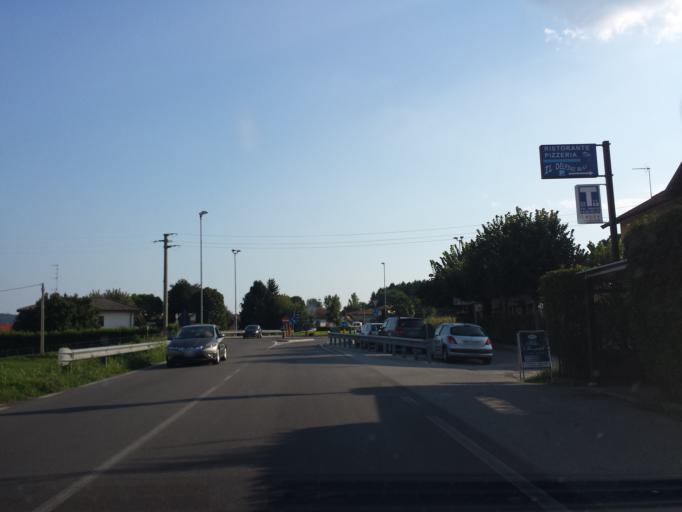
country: IT
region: Lombardy
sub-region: Provincia di Varese
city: Angera
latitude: 45.7867
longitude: 8.5943
